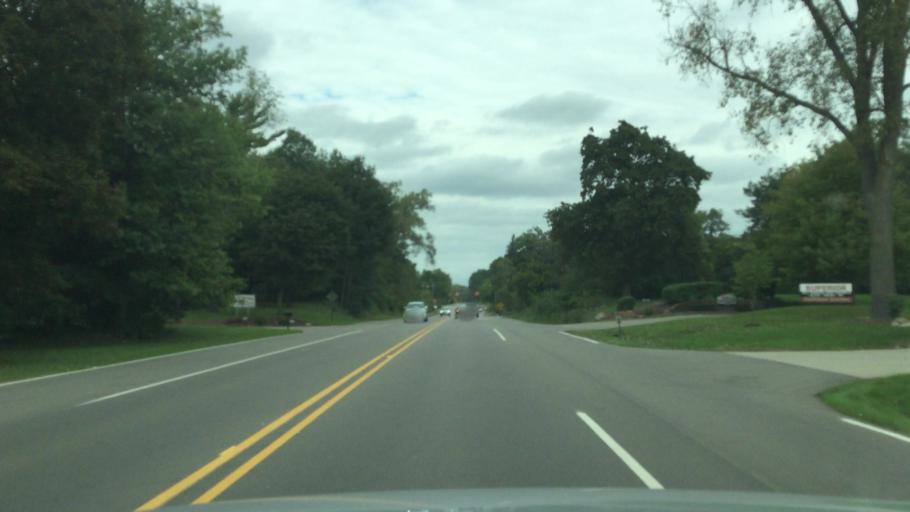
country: US
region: Michigan
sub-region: Livingston County
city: Brighton
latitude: 42.5493
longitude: -83.7519
